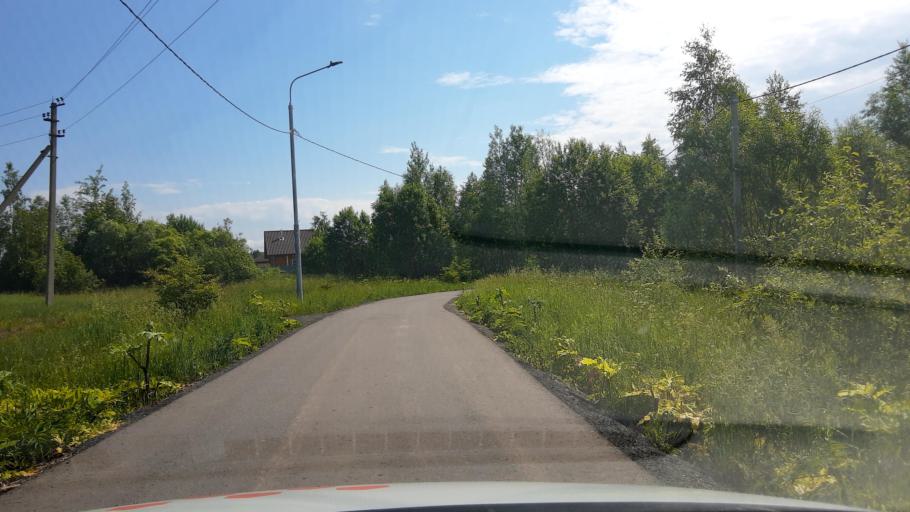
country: RU
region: Moskovskaya
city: Kievskij
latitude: 55.2239
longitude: 36.9800
